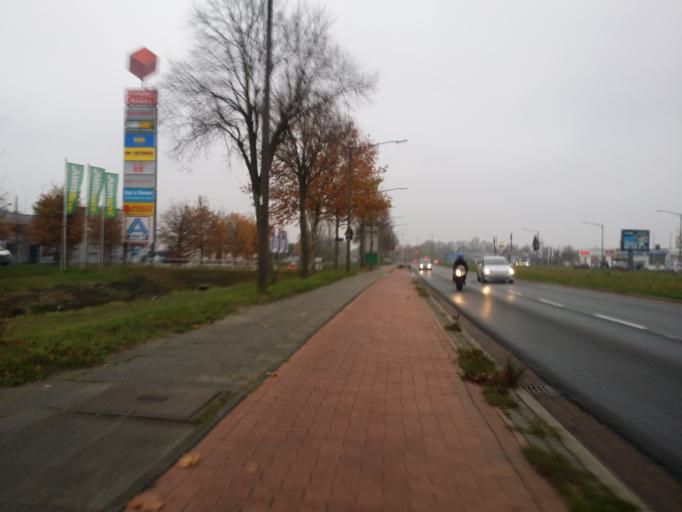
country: DE
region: Bremen
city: Bremen
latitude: 53.0488
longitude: 8.8474
